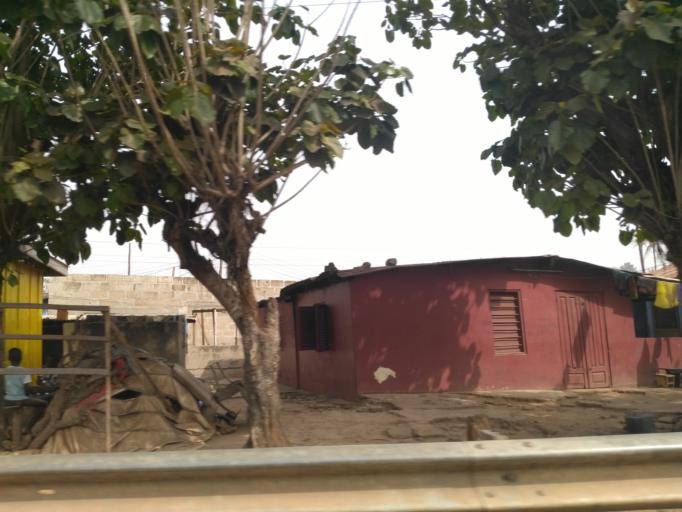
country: GH
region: Ashanti
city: Kumasi
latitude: 6.6696
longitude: -1.6314
